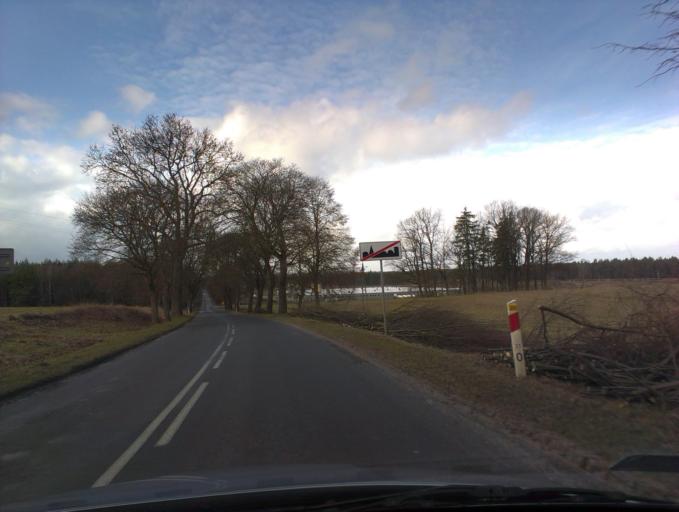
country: PL
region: Pomeranian Voivodeship
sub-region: Powiat czluchowski
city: Rzeczenica
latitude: 53.6536
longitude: 17.1408
